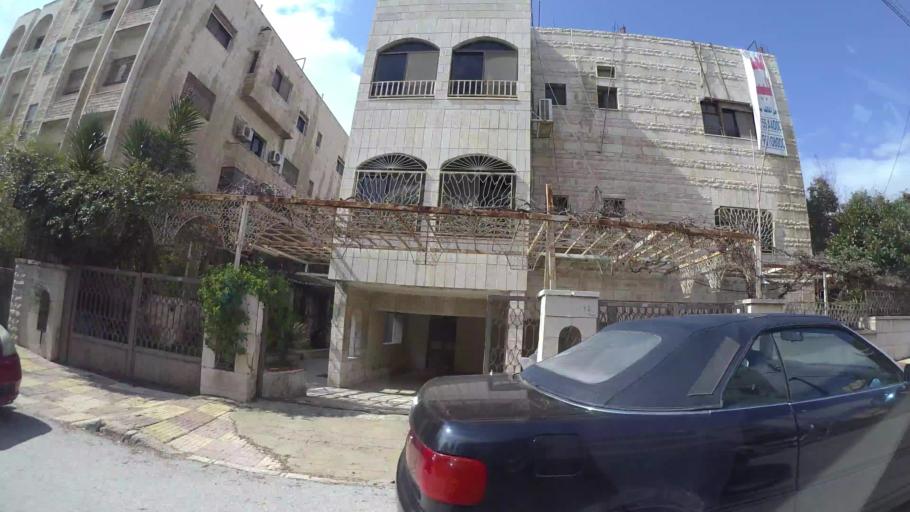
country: JO
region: Amman
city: Amman
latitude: 31.9798
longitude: 35.8989
